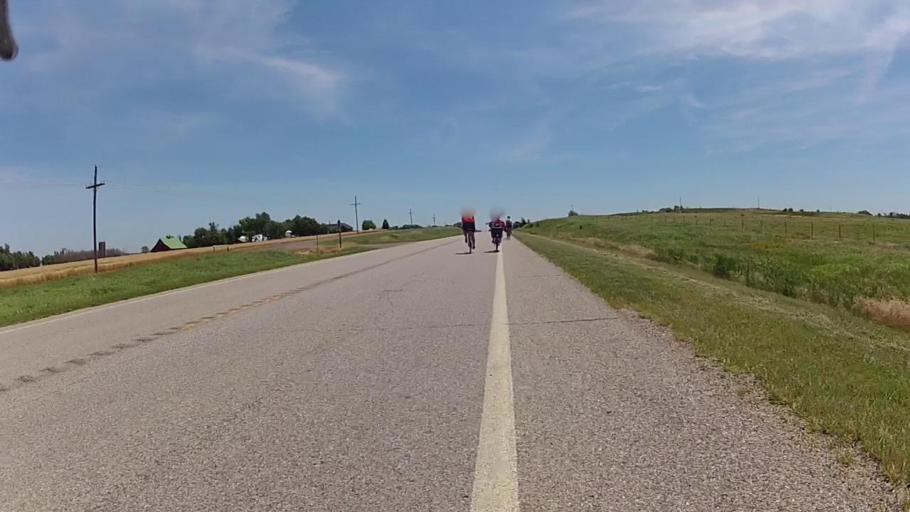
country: US
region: Kansas
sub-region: Barber County
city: Medicine Lodge
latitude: 37.2536
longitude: -98.4803
